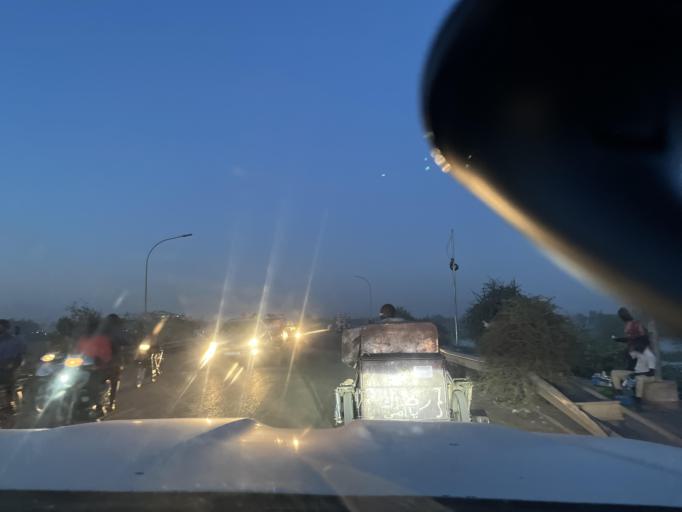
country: TD
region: Chari-Baguirmi
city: N'Djamena
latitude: 12.0881
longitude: 15.1089
